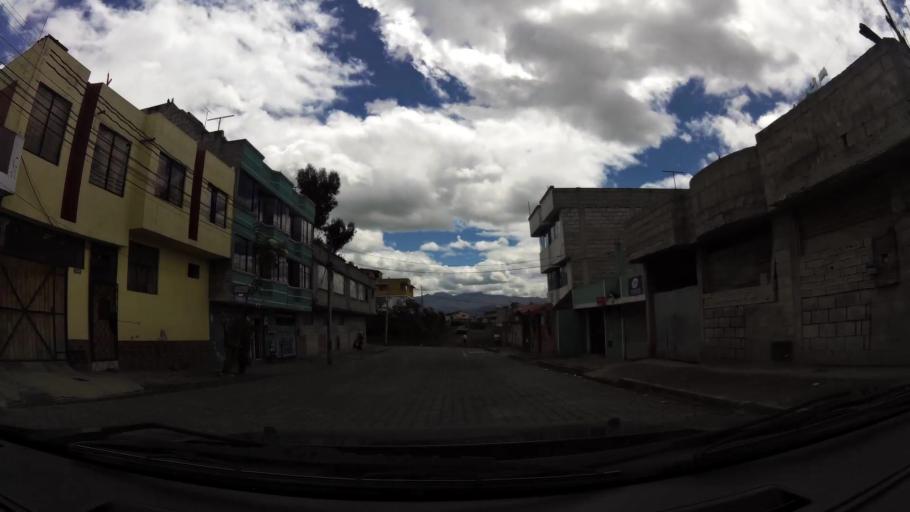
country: EC
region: Pichincha
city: Sangolqui
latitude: -0.3400
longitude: -78.5577
